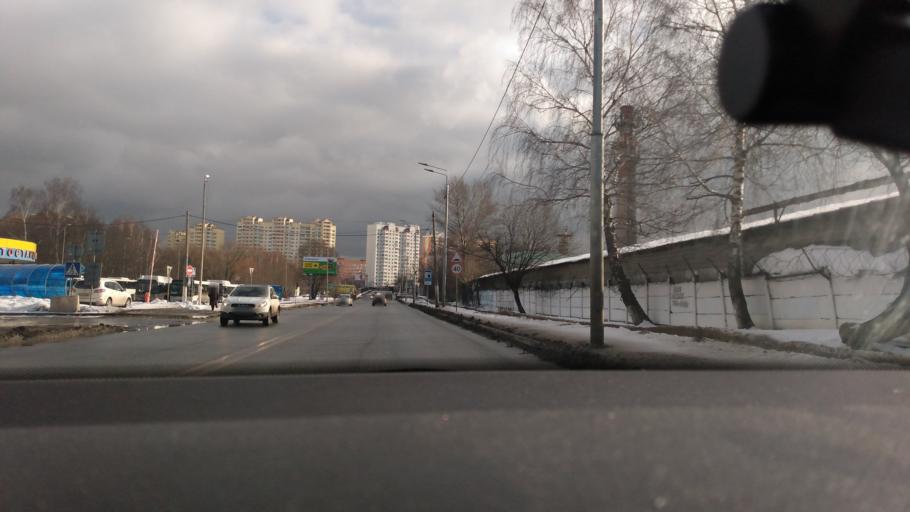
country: RU
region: Moskovskaya
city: Balashikha
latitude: 55.8317
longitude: 37.9487
